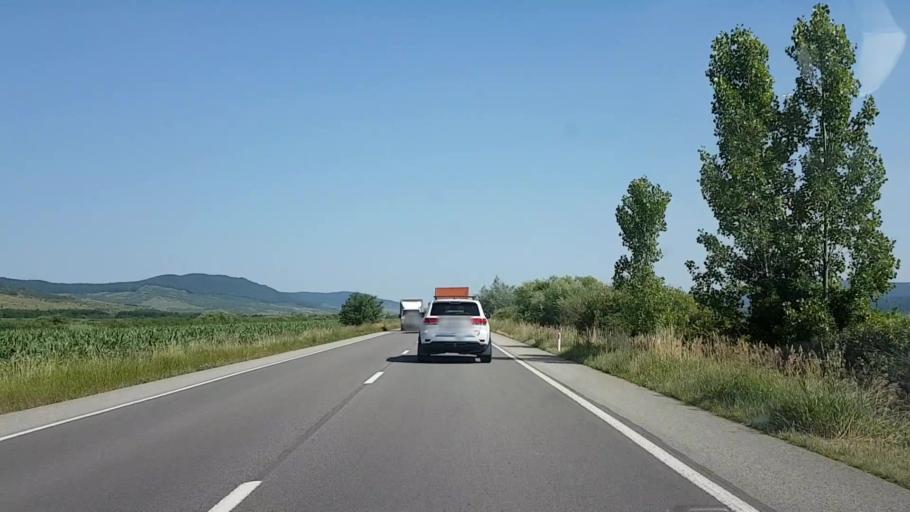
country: RO
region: Bistrita-Nasaud
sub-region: Comuna Sieu-Odorhei
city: Sieu-Odorhei
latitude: 47.1232
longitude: 24.3238
